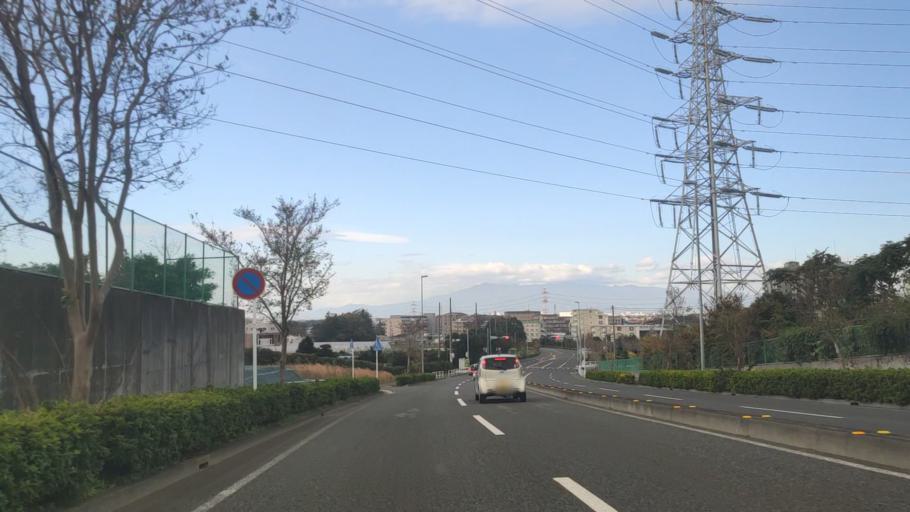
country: JP
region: Kanagawa
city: Minami-rinkan
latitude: 35.4283
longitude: 139.5003
